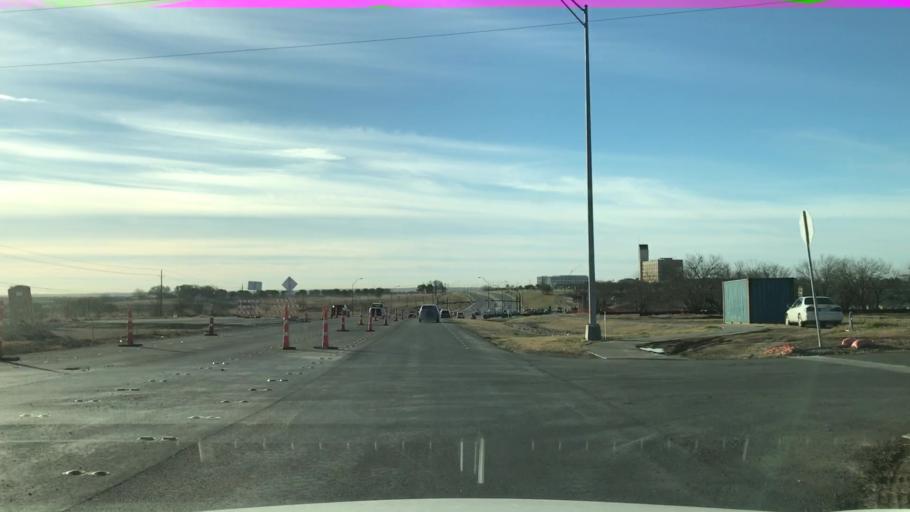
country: US
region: Texas
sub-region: Williamson County
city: Georgetown
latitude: 30.5767
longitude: -97.6518
